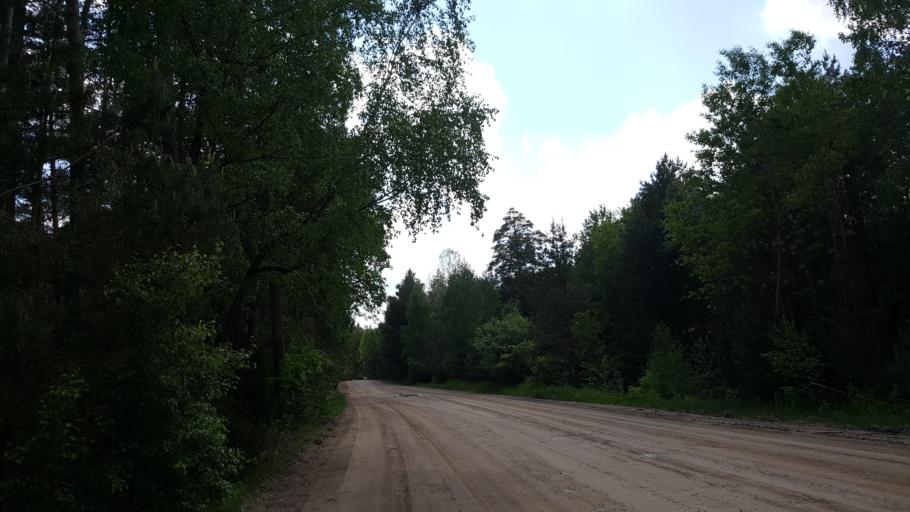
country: BY
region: Brest
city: Kamyanyets
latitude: 52.4392
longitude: 23.9750
